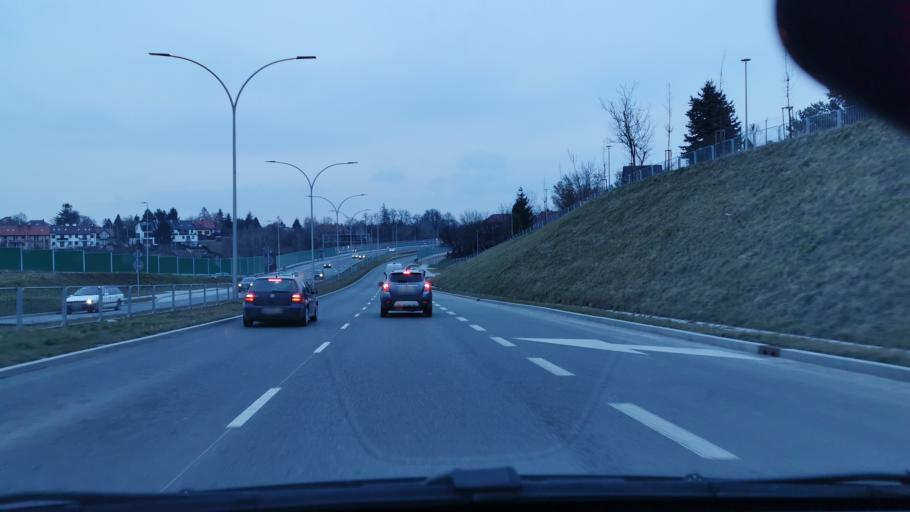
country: PL
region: Lublin Voivodeship
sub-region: Powiat lubelski
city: Lublin
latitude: 51.2522
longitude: 22.5051
